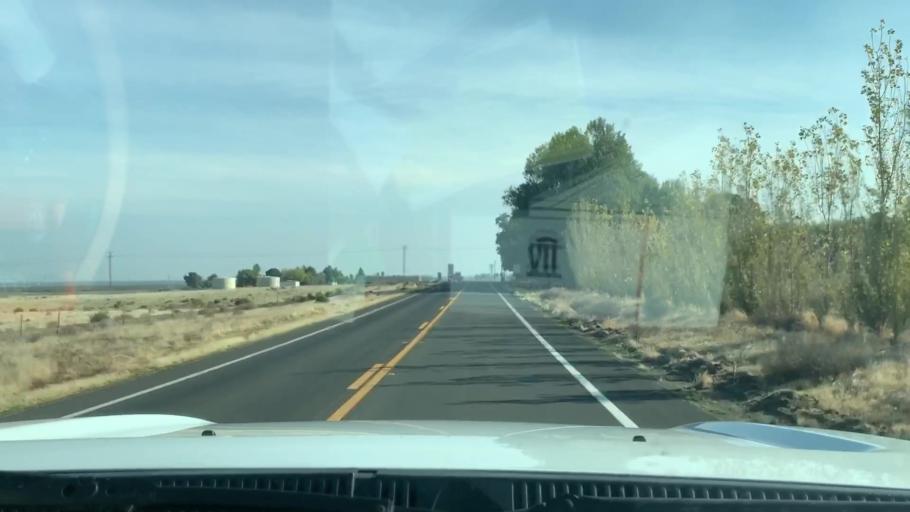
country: US
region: California
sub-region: Fresno County
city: Coalinga
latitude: 36.2542
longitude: -120.2581
